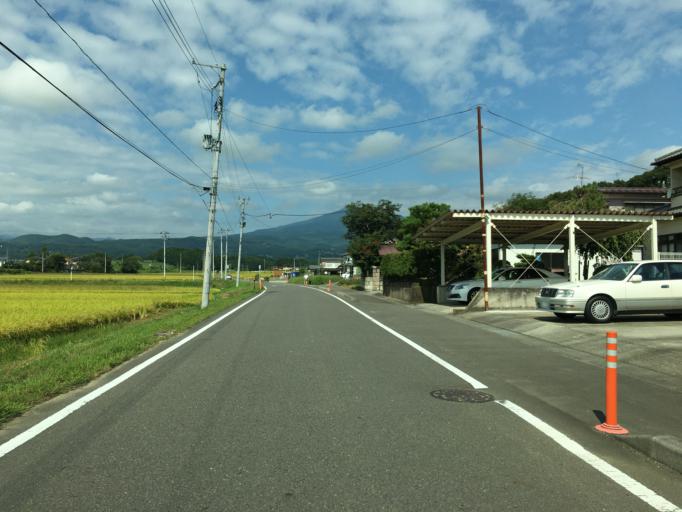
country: JP
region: Fukushima
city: Motomiya
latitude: 37.5359
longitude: 140.3700
